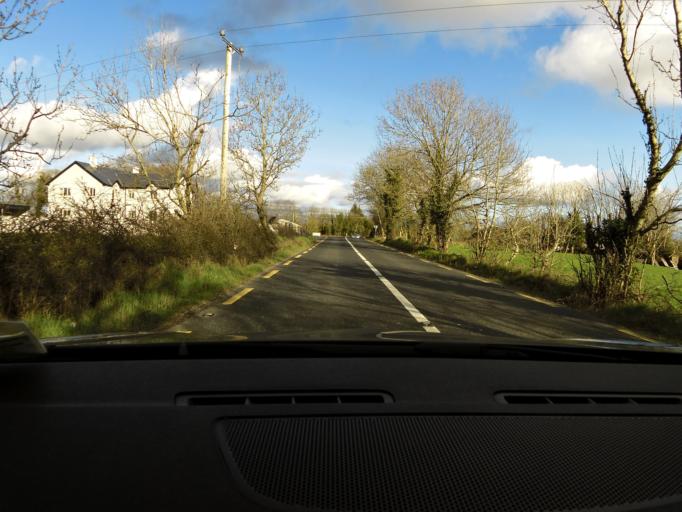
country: IE
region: Connaught
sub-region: Roscommon
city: Roscommon
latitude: 53.6616
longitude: -8.2812
